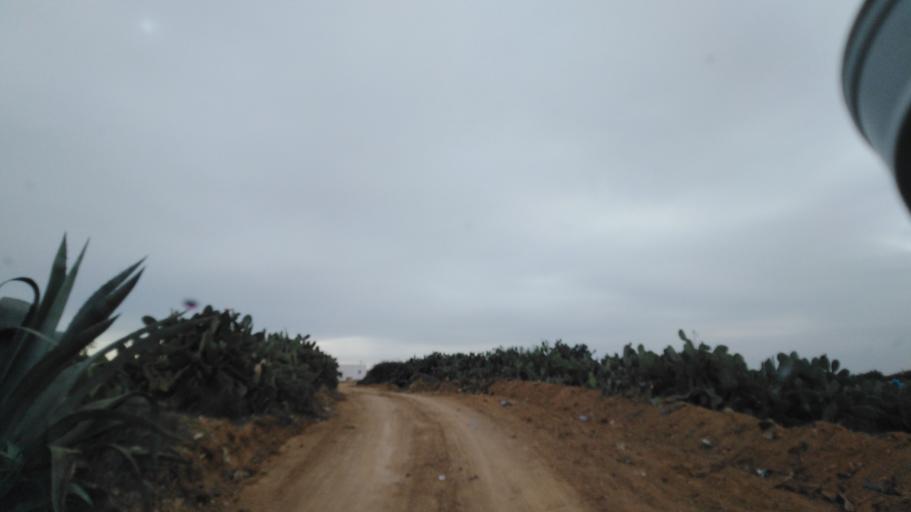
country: TN
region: Safaqis
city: Bi'r `Ali Bin Khalifah
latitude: 34.7661
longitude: 10.3763
